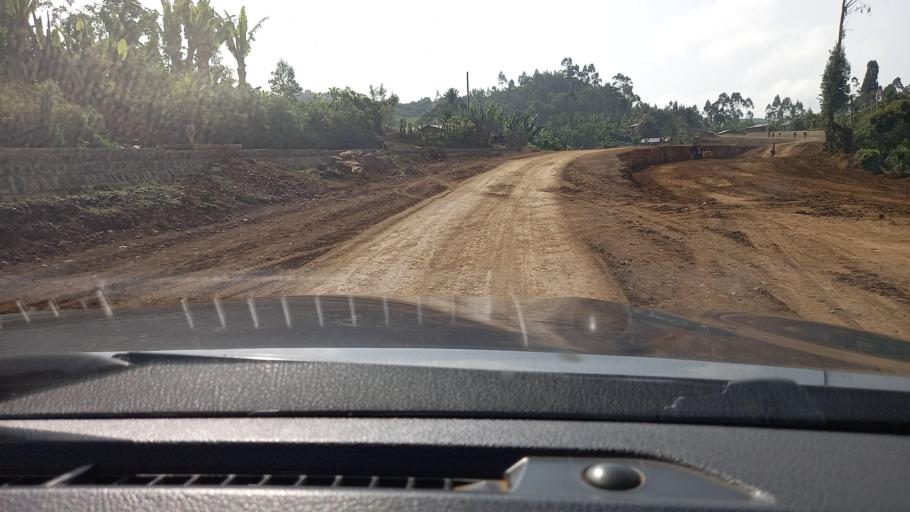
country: ET
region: Southern Nations, Nationalities, and People's Region
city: Mizan Teferi
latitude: 6.1644
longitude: 35.5928
